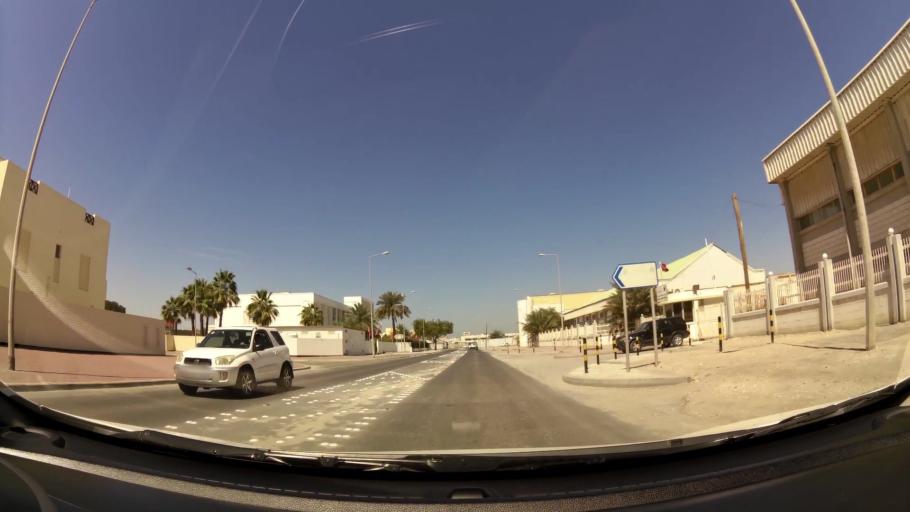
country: BH
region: Muharraq
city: Al Muharraq
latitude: 26.2717
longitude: 50.6145
